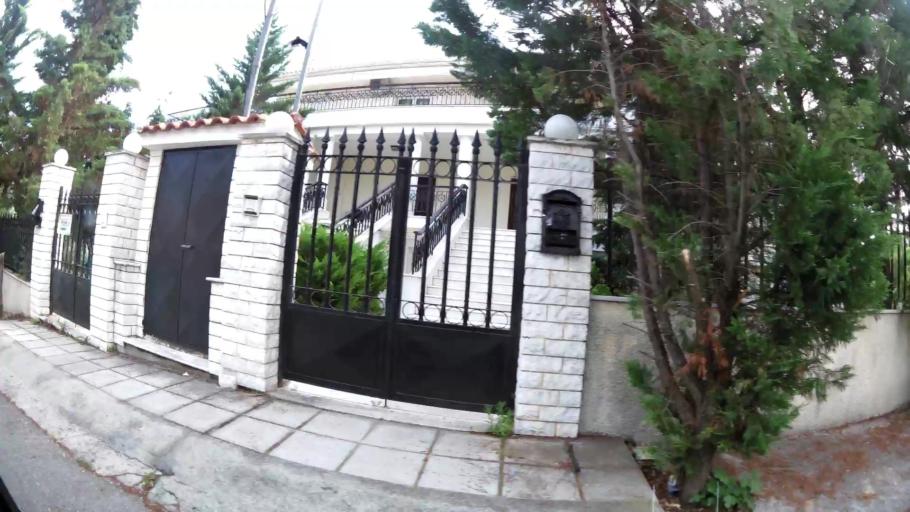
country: GR
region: Central Macedonia
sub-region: Nomos Thessalonikis
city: Panorama
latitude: 40.5846
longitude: 23.0248
